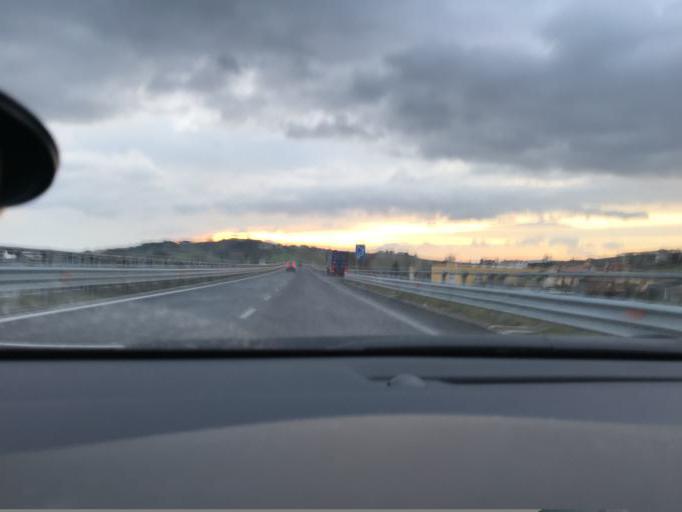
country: IT
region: Umbria
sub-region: Provincia di Perugia
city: Petrignano
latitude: 43.1369
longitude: 12.5327
